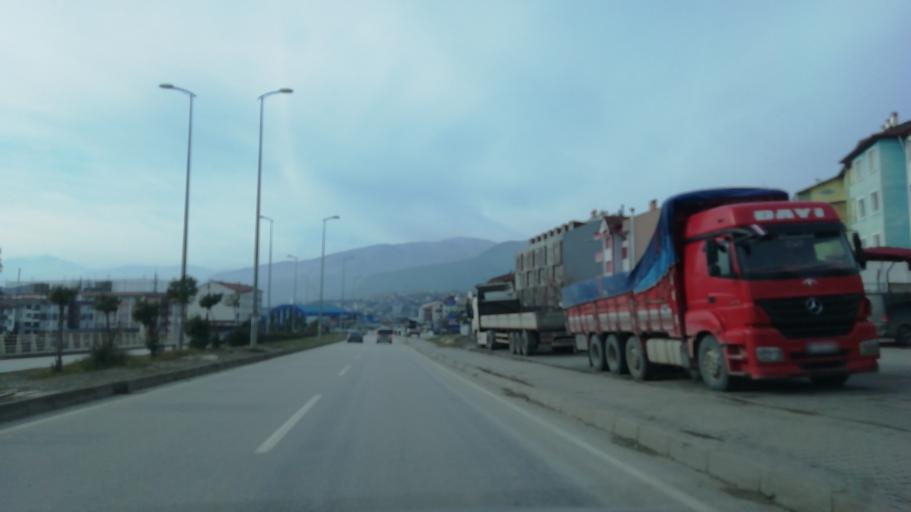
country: TR
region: Karabuk
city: Karabuk
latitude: 41.2173
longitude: 32.6643
